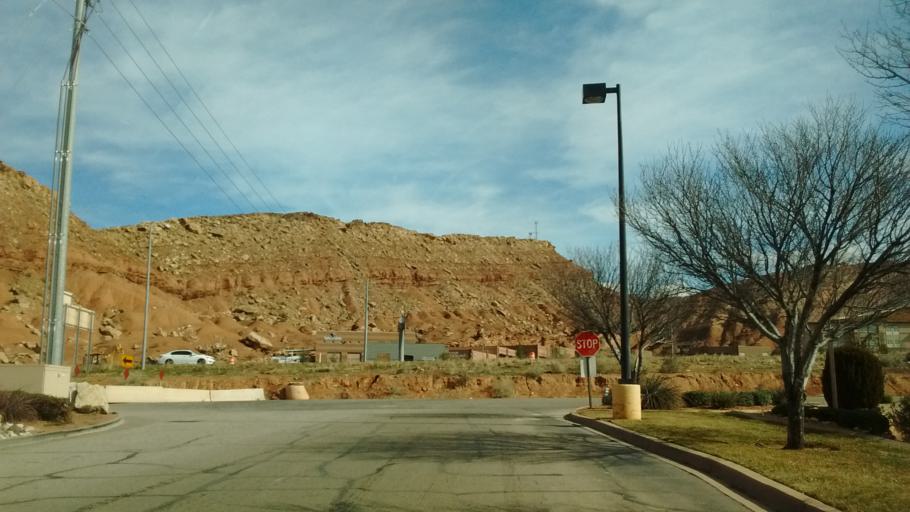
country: US
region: Utah
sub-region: Washington County
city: Saint George
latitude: 37.0645
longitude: -113.5850
